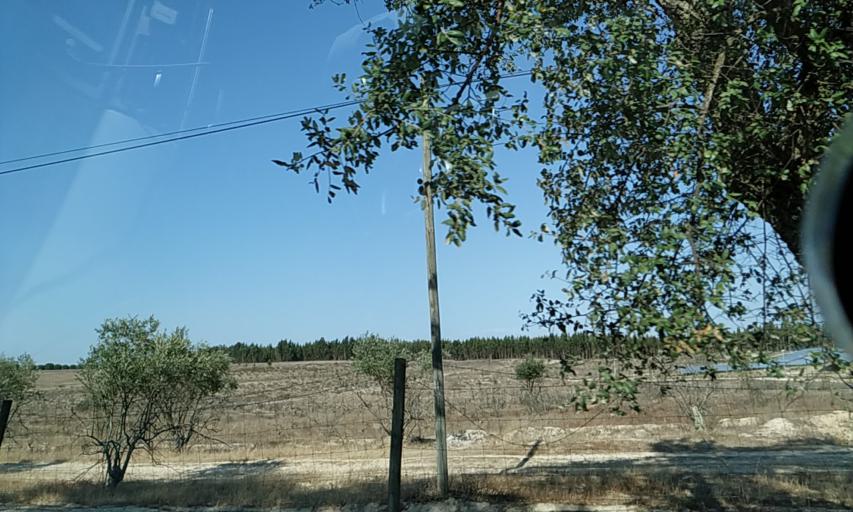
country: PT
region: Evora
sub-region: Vendas Novas
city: Vendas Novas
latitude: 38.7307
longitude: -8.6233
